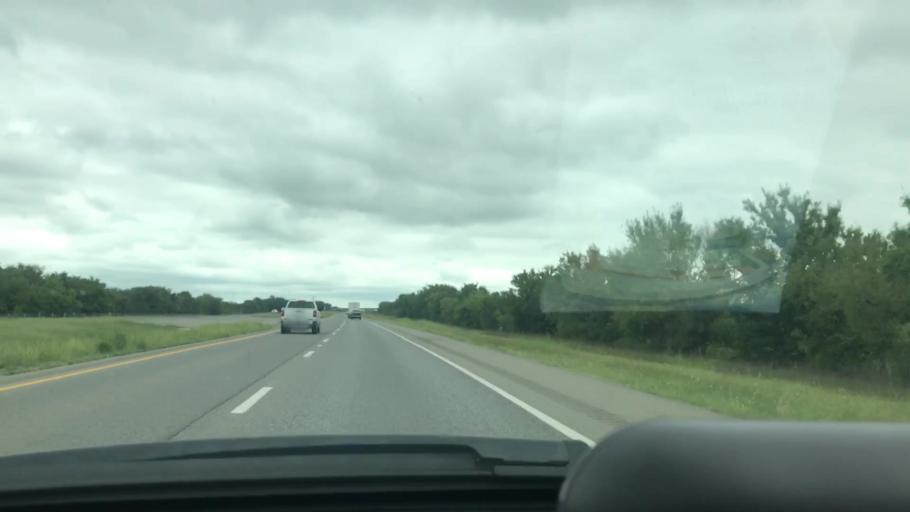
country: US
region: Oklahoma
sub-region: McIntosh County
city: Eufaula
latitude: 35.3808
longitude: -95.5681
